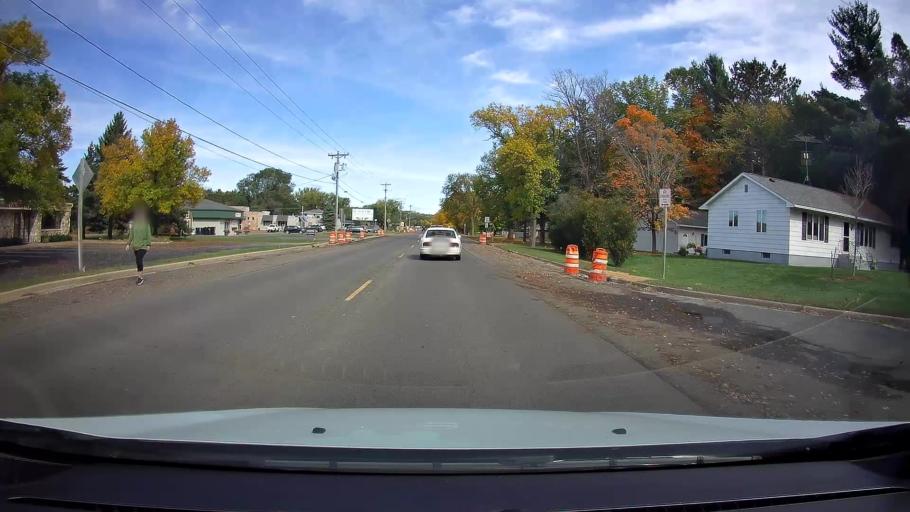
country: US
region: Wisconsin
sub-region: Polk County
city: Saint Croix Falls
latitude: 45.3556
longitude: -92.6371
